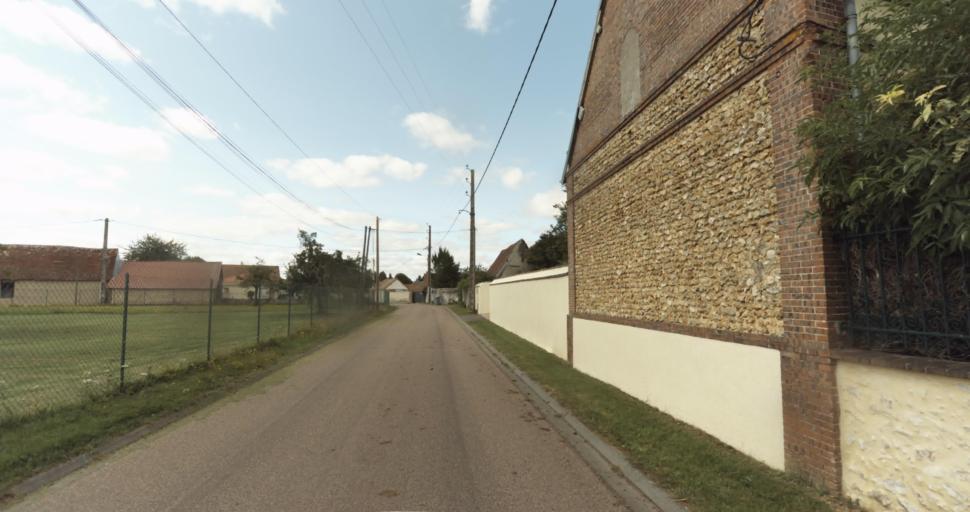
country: FR
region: Haute-Normandie
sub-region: Departement de l'Eure
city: La Madeleine-de-Nonancourt
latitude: 48.8282
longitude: 1.1783
